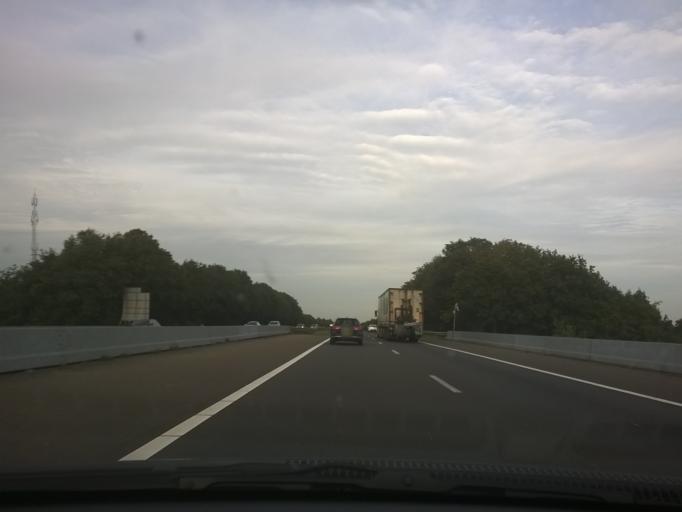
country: NL
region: Groningen
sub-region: Gemeente Leek
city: Leek
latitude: 53.1850
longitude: 6.3789
